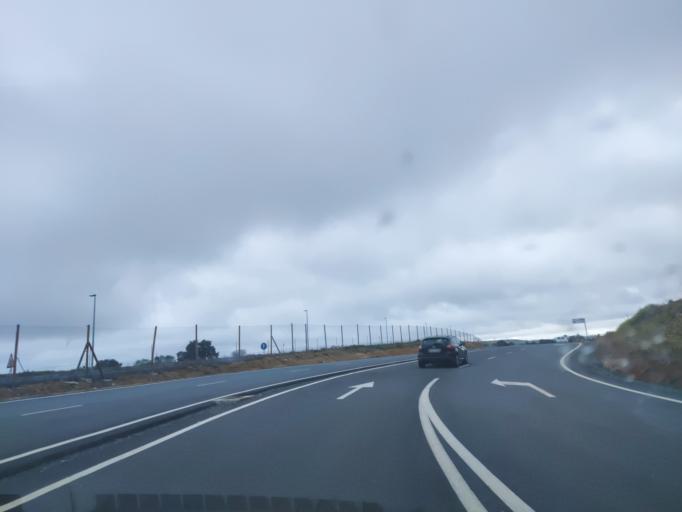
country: ES
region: Castille-La Mancha
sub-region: Province of Toledo
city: Toledo
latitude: 39.8410
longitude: -4.0854
